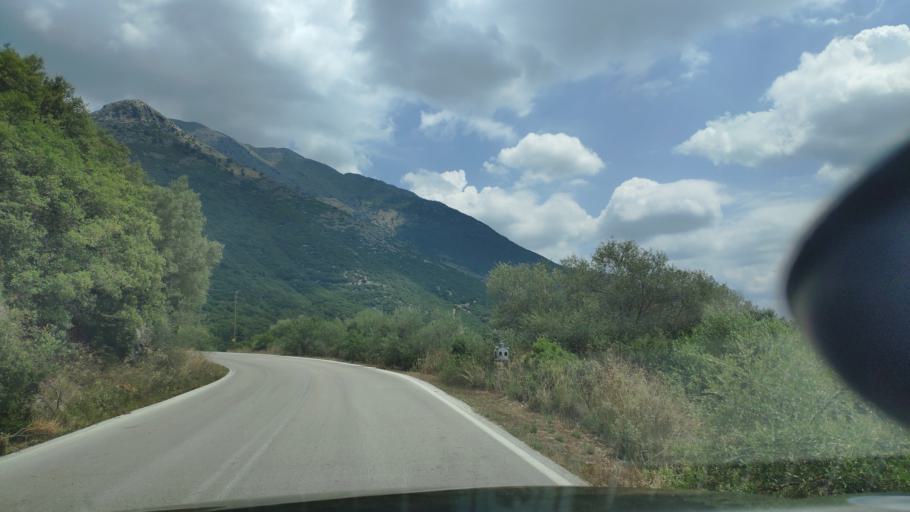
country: GR
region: Epirus
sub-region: Nomos Artas
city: Kampi
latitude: 39.2689
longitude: 20.9297
